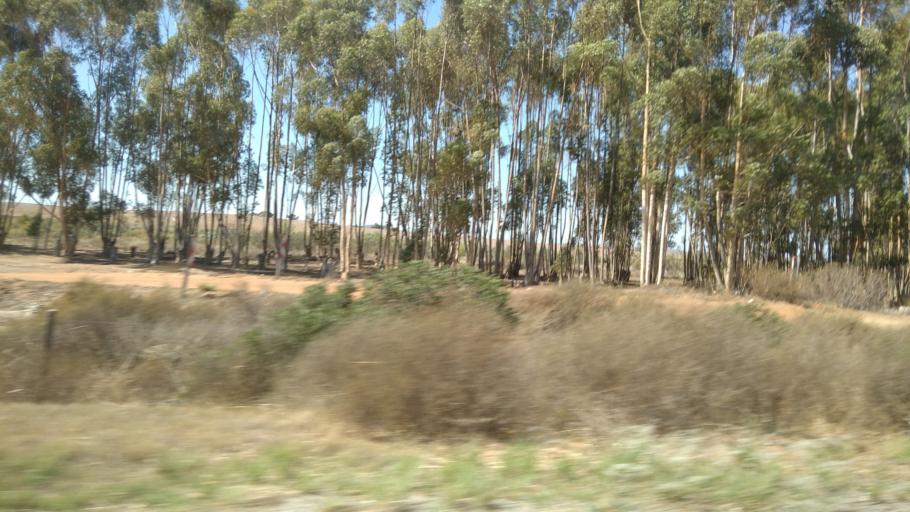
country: ZA
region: Western Cape
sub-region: West Coast District Municipality
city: Moorreesburg
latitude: -33.2462
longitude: 18.5773
